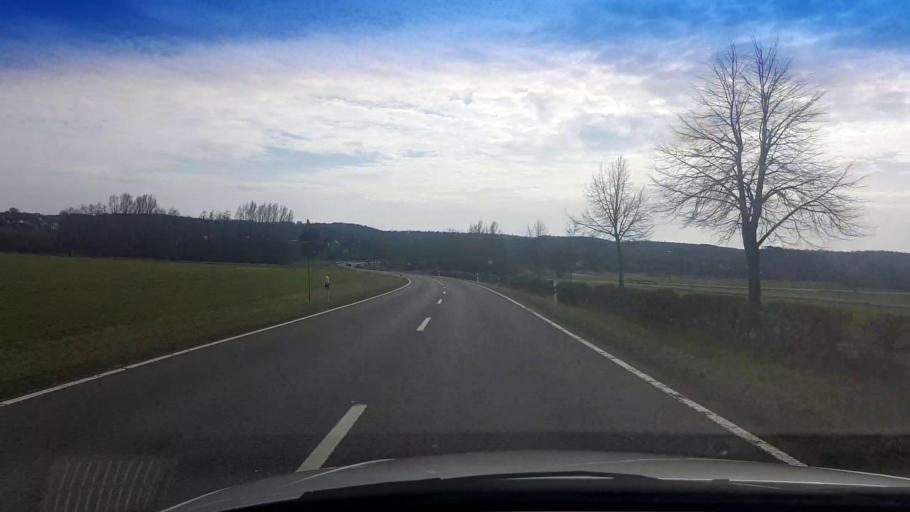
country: DE
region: Bavaria
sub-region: Upper Franconia
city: Frensdorf
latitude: 49.8246
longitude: 10.8657
